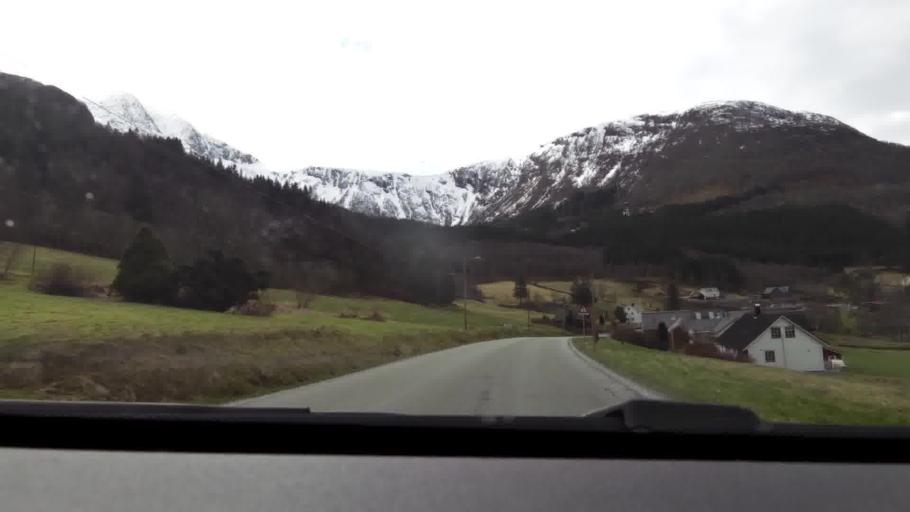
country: NO
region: More og Romsdal
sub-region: Gjemnes
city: Batnfjordsora
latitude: 62.9270
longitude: 7.5973
